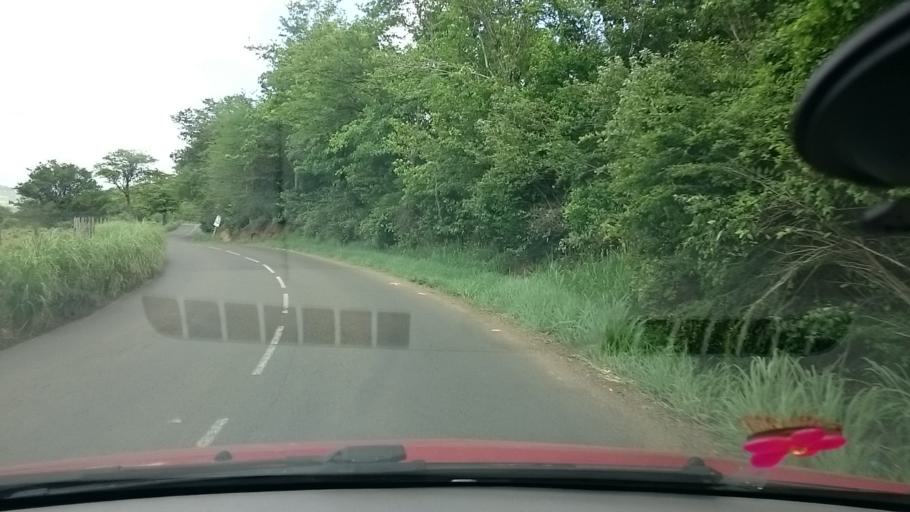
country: MQ
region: Martinique
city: Petite Riviere Salee
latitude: 14.7566
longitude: -60.9296
